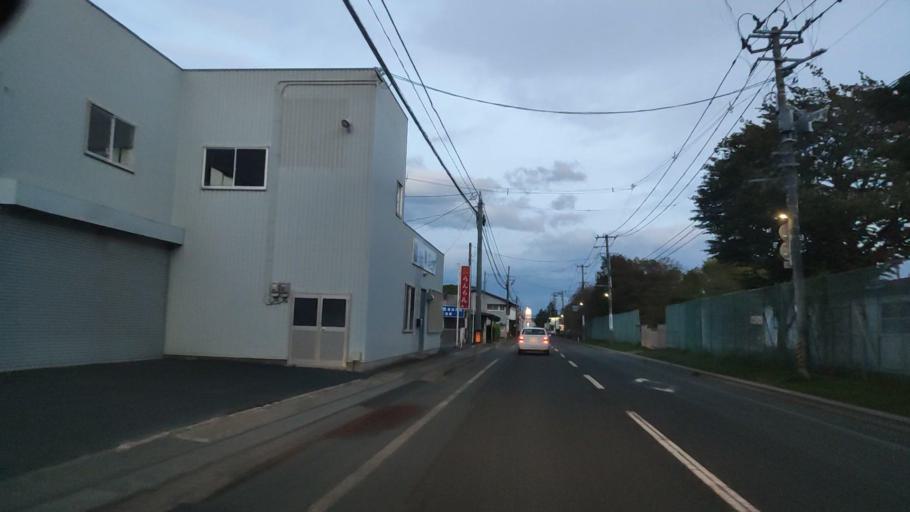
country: JP
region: Iwate
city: Morioka-shi
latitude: 39.7191
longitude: 141.1218
